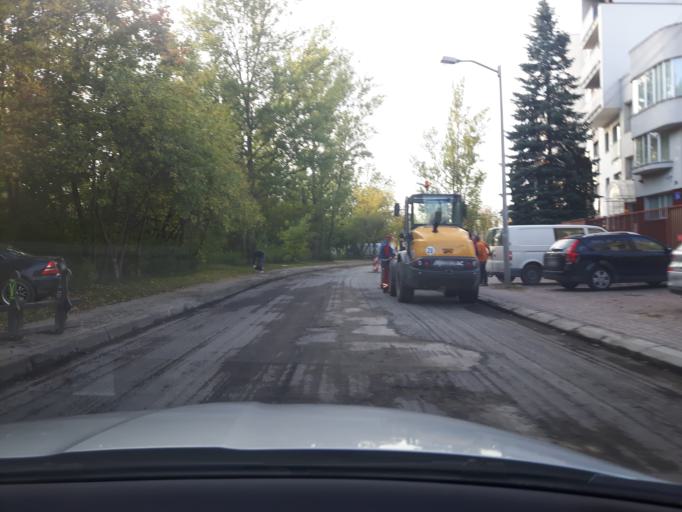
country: PL
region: Masovian Voivodeship
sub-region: Warszawa
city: Mokotow
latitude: 52.1658
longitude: 20.9939
